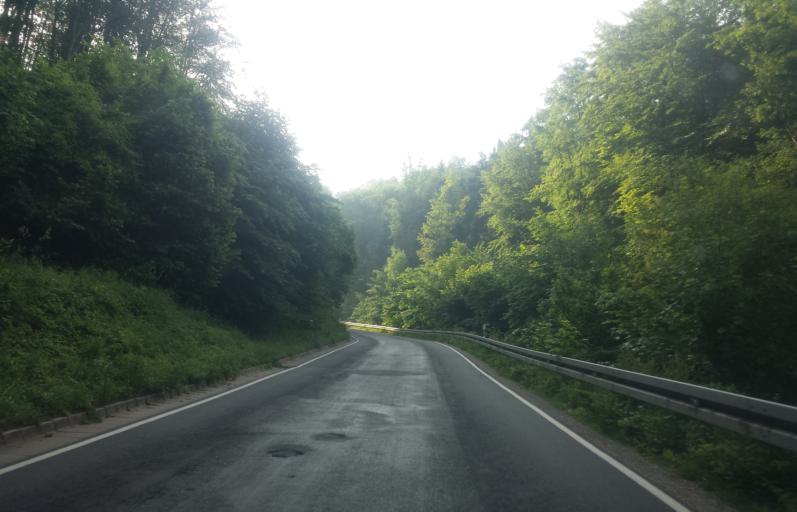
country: DE
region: Bavaria
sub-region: Upper Franconia
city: Ebermannstadt
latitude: 49.7835
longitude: 11.2137
